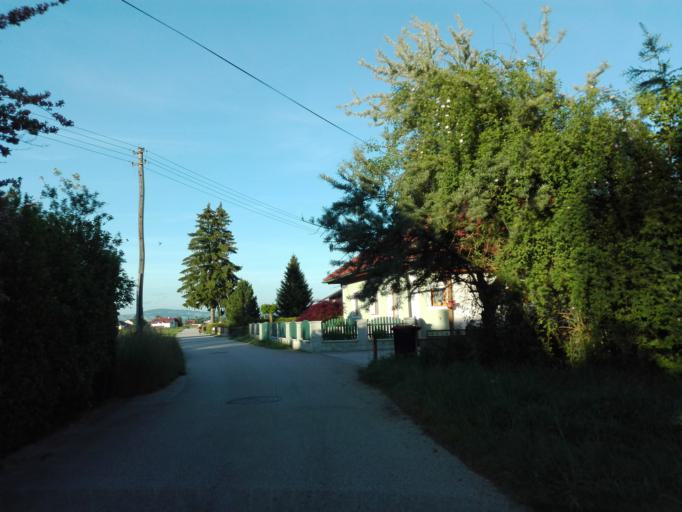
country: AT
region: Upper Austria
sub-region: Politischer Bezirk Urfahr-Umgebung
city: Goldworth
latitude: 48.2847
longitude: 14.0690
